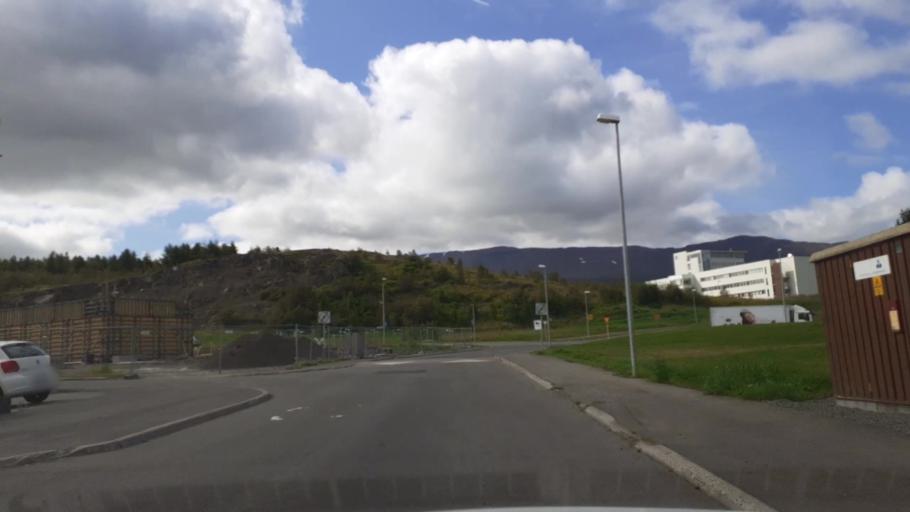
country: IS
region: Northeast
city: Akureyri
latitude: 65.6848
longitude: -18.1138
